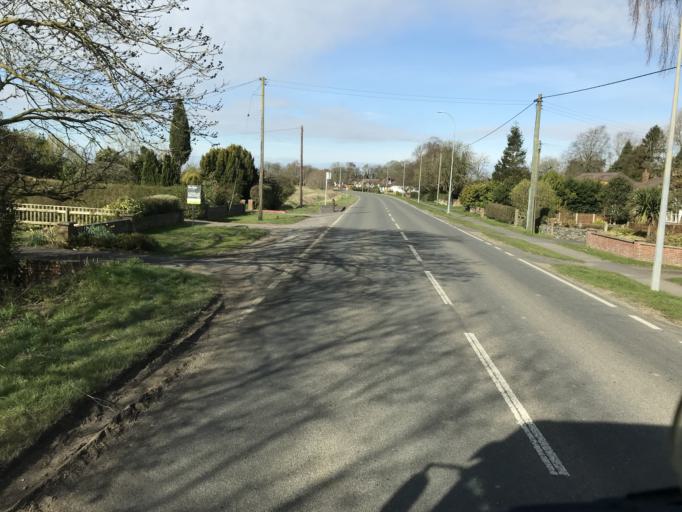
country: GB
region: England
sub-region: Lincolnshire
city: Market Rasen
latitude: 53.3884
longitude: -0.3486
